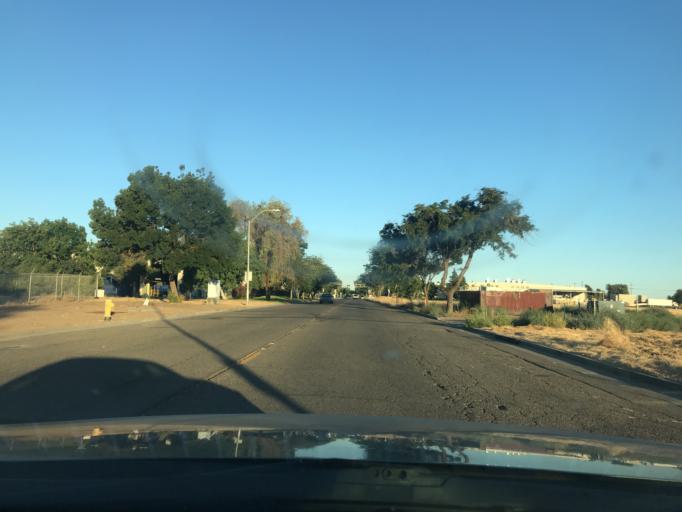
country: US
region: California
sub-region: Merced County
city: Merced
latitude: 37.3164
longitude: -120.5118
